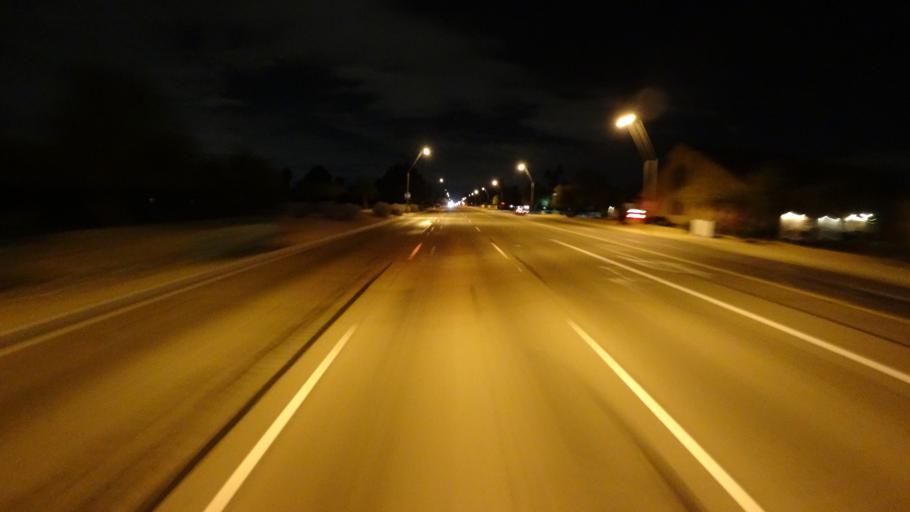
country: US
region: Arizona
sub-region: Maricopa County
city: Guadalupe
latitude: 33.3280
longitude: -111.9284
